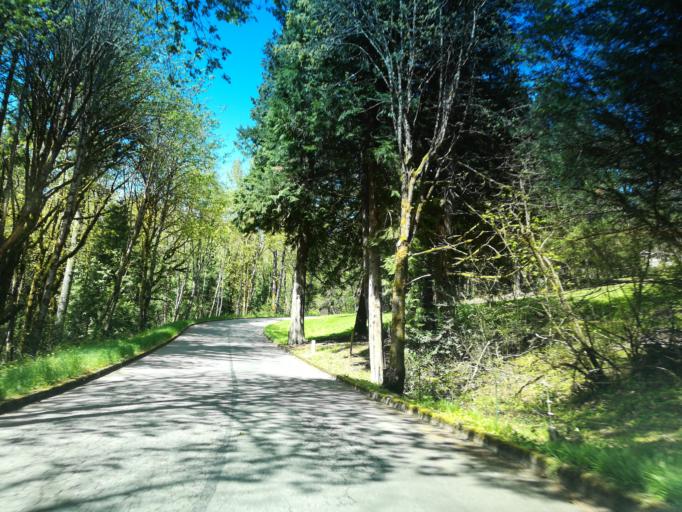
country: US
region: Oregon
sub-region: Multnomah County
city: Gresham
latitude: 45.4563
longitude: -122.4271
